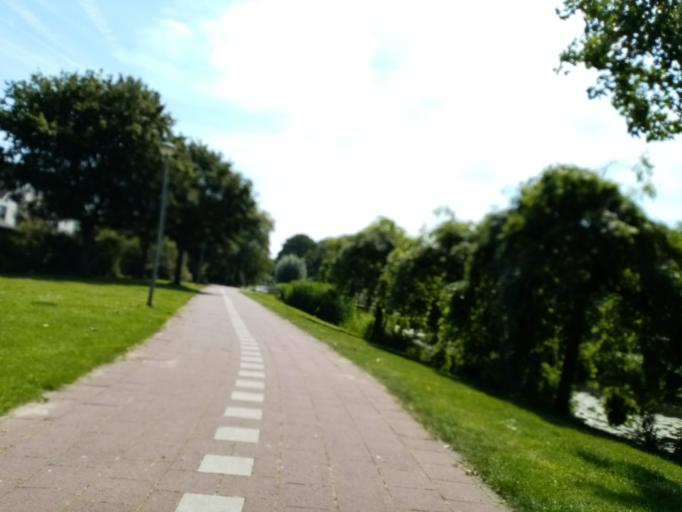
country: NL
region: South Holland
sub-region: Gemeente Katwijk
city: Katwijk aan den Rijn
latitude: 52.2081
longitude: 4.4290
